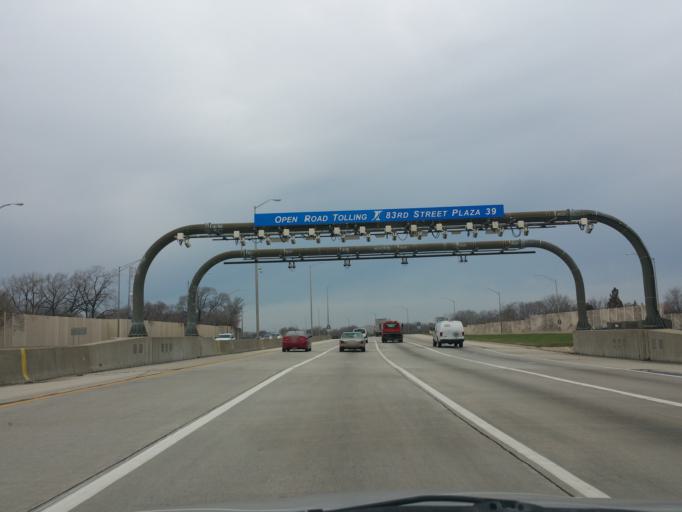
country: US
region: Illinois
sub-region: Cook County
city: Justice
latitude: 41.7391
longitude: -87.8260
